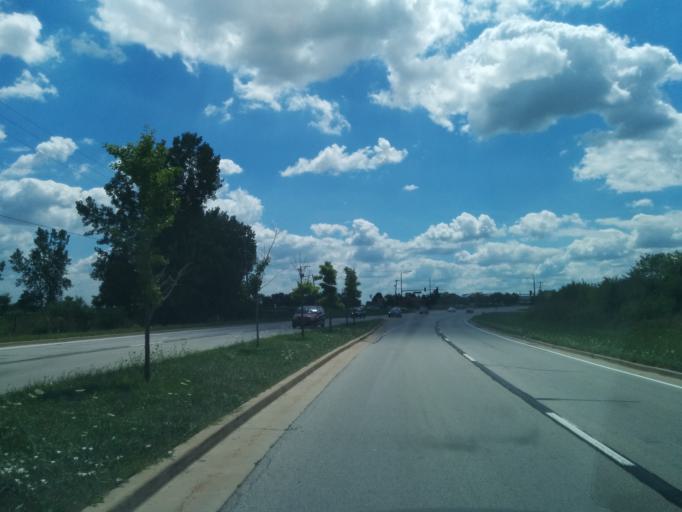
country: US
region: Illinois
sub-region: Will County
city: Plainfield
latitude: 41.6833
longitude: -88.1661
